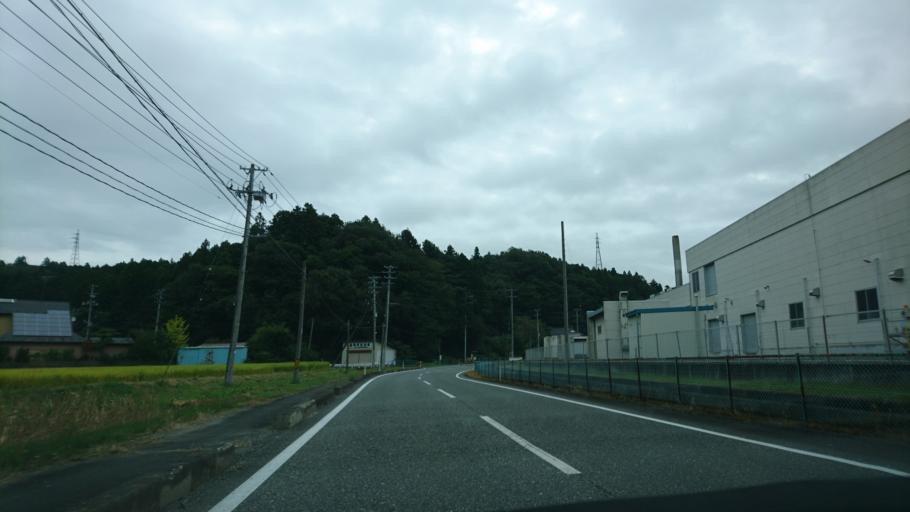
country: JP
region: Iwate
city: Ichinoseki
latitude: 38.8100
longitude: 141.0823
